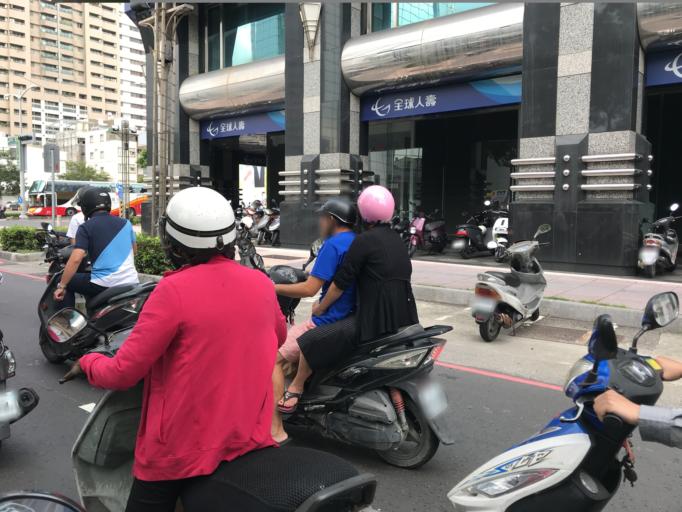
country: TW
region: Kaohsiung
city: Kaohsiung
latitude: 22.6301
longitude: 120.3137
